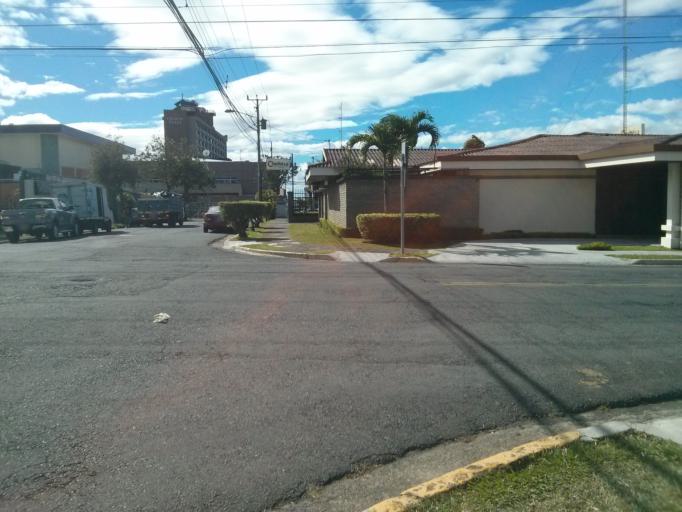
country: CR
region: San Jose
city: San Jose
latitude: 9.9396
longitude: -84.0965
